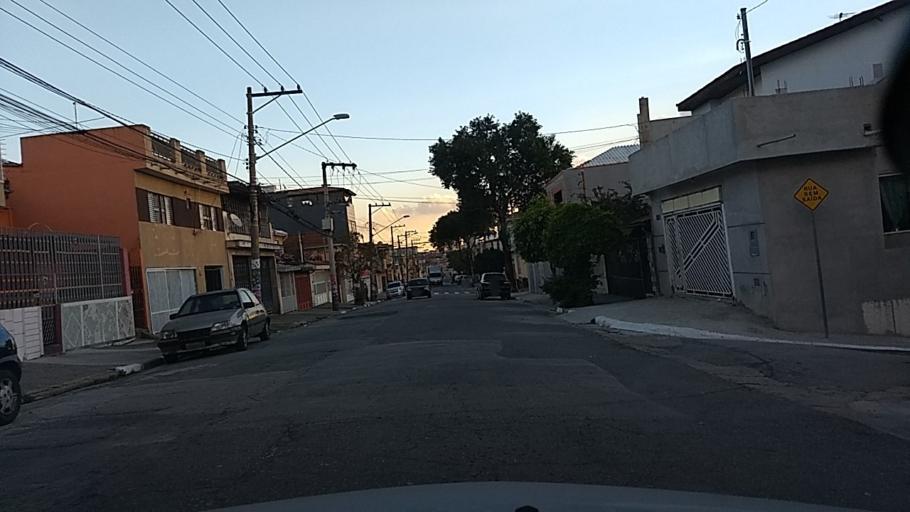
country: BR
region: Sao Paulo
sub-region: Guarulhos
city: Guarulhos
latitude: -23.4853
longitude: -46.5833
